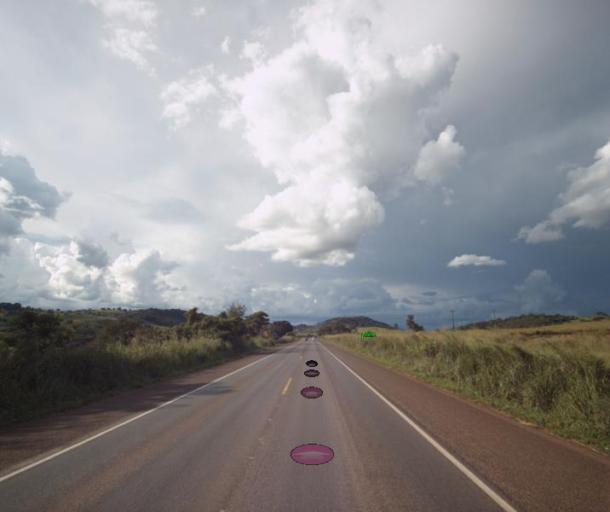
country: BR
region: Goias
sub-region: Rialma
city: Rialma
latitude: -15.3012
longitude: -49.5702
